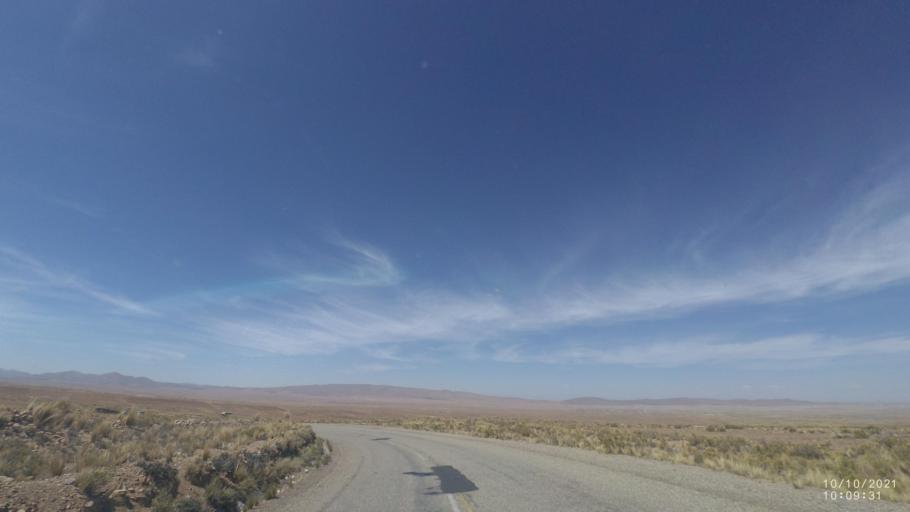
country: BO
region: La Paz
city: Eucaliptus
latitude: -17.4005
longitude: -67.4892
